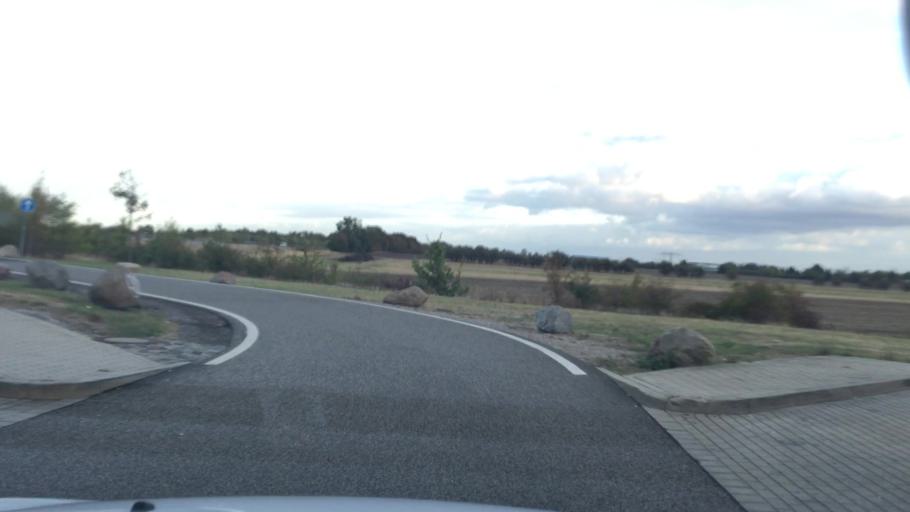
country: DE
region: Saxony-Anhalt
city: Grobers
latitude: 51.4552
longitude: 12.1088
